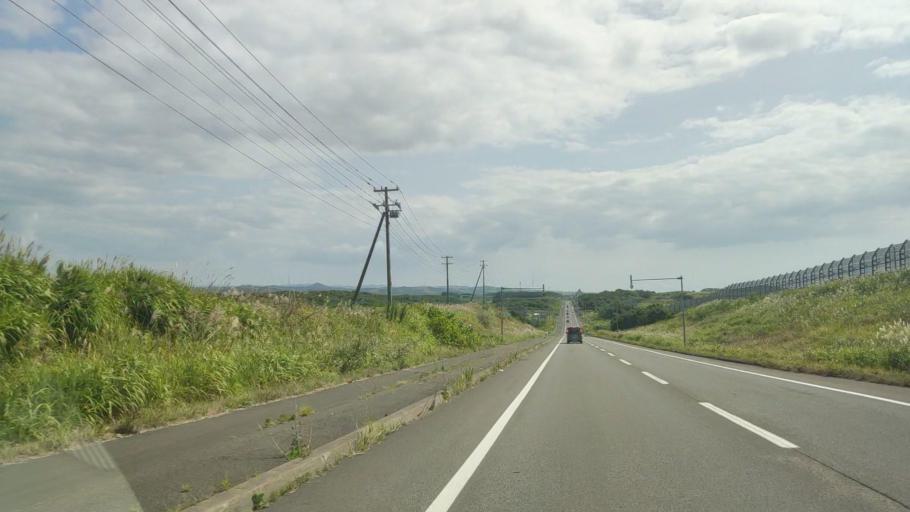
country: JP
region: Hokkaido
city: Rumoi
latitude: 44.2999
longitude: 141.6530
